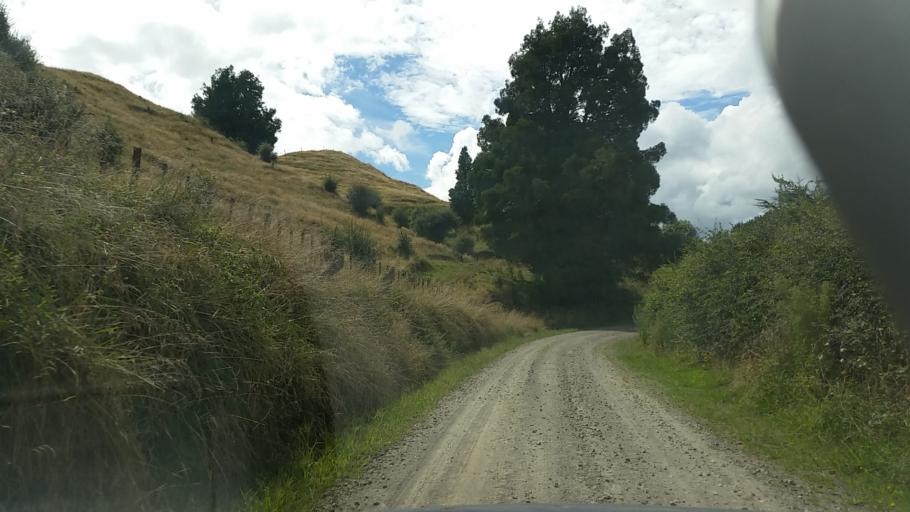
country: NZ
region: Taranaki
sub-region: South Taranaki District
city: Eltham
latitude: -39.2570
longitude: 174.5676
